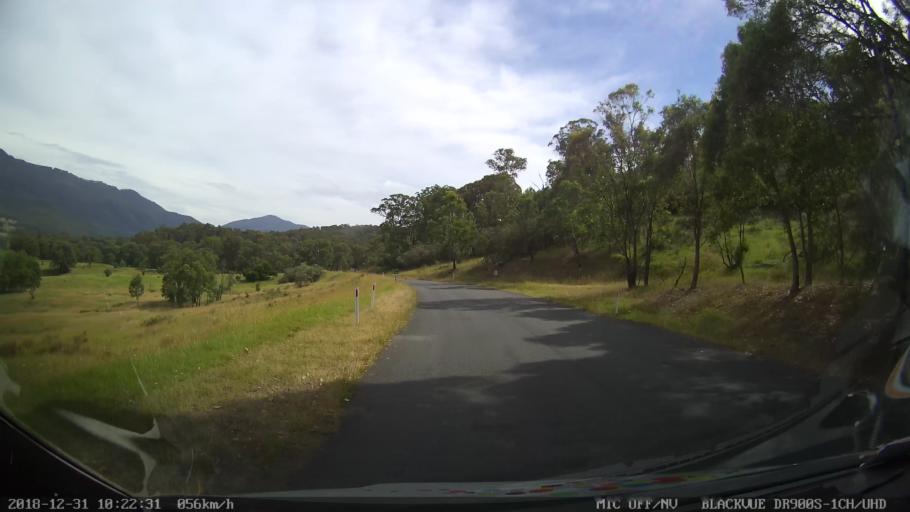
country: AU
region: New South Wales
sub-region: Snowy River
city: Jindabyne
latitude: -36.5249
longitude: 148.1432
